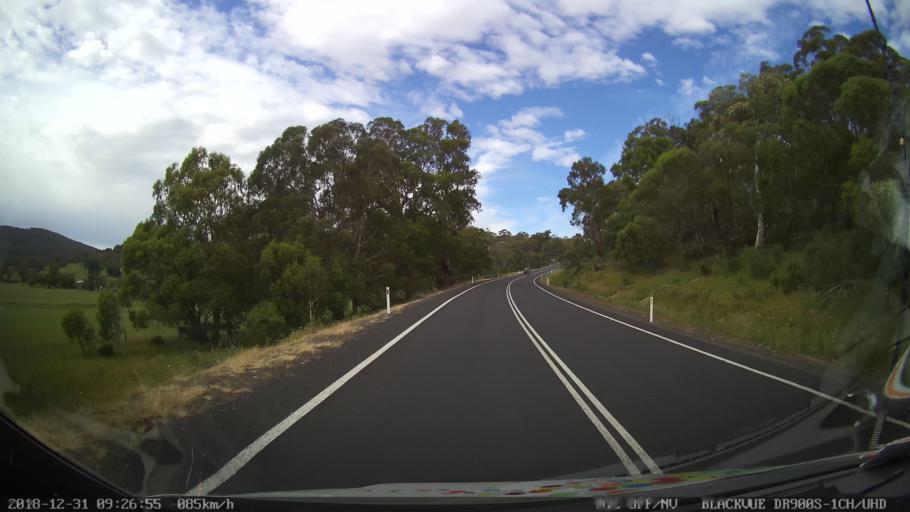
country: AU
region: New South Wales
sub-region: Snowy River
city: Jindabyne
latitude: -36.4533
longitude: 148.4918
